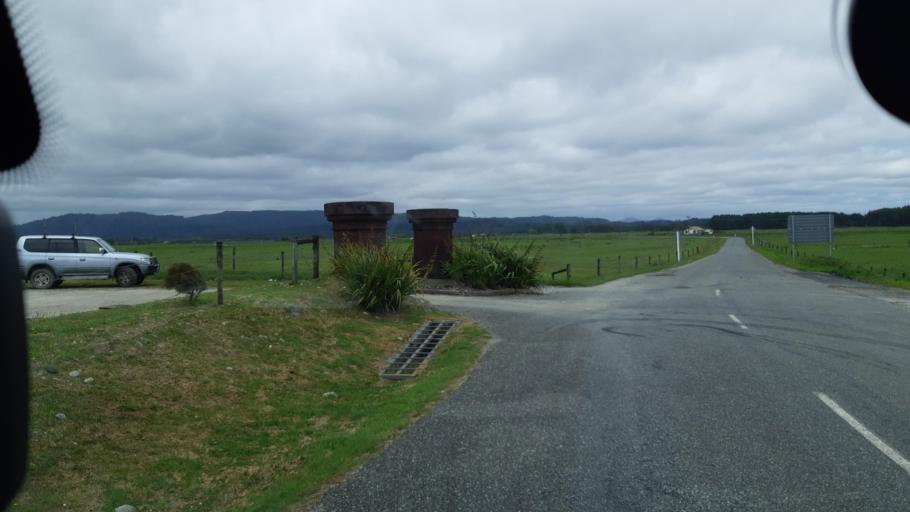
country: NZ
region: West Coast
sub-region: Westland District
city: Hokitika
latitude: -42.6735
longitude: 171.0249
